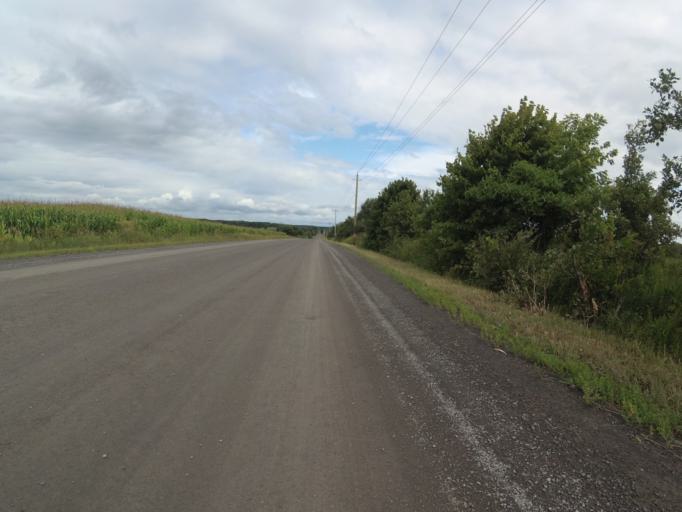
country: CA
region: Ontario
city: Clarence-Rockland
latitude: 45.4575
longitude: -75.2963
